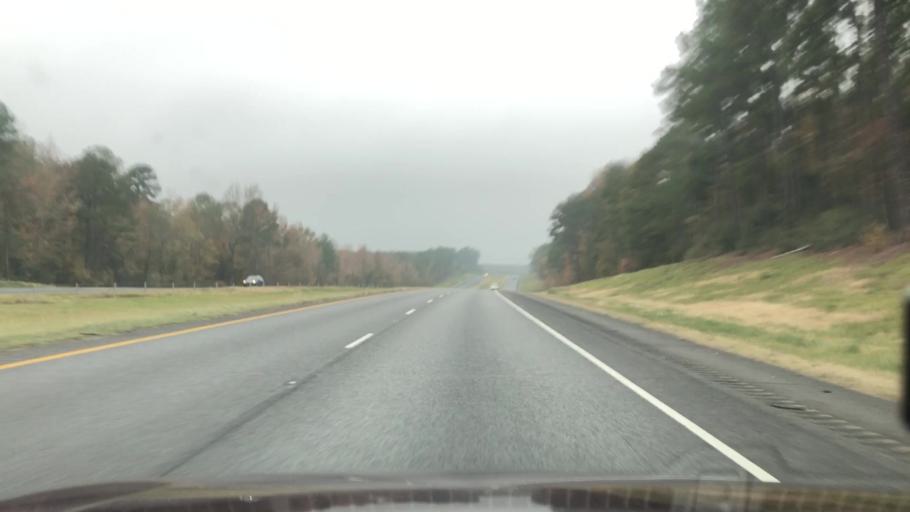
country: US
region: Louisiana
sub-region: Lincoln Parish
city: Ruston
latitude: 32.5224
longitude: -92.4177
